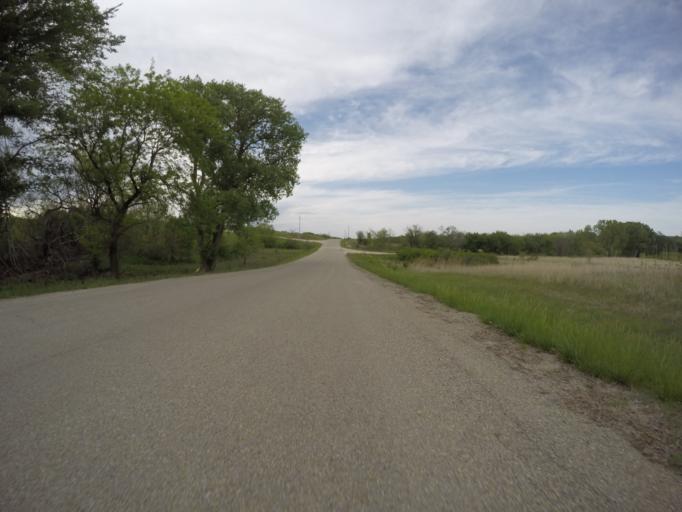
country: US
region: Kansas
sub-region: Riley County
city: Ogden
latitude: 39.0058
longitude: -96.6022
